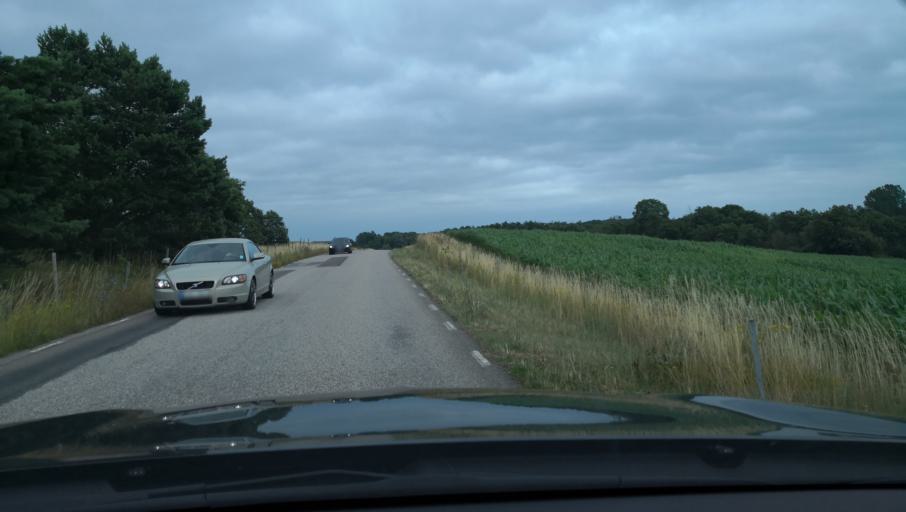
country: SE
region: Skane
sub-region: Simrishamns Kommun
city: Kivik
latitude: 55.6983
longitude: 14.1867
